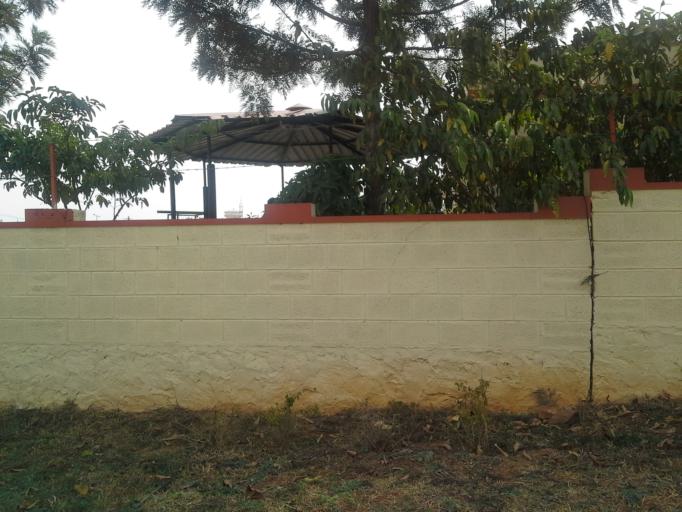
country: IN
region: Karnataka
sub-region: Mysore
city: Mysore
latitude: 12.3548
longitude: 76.6140
